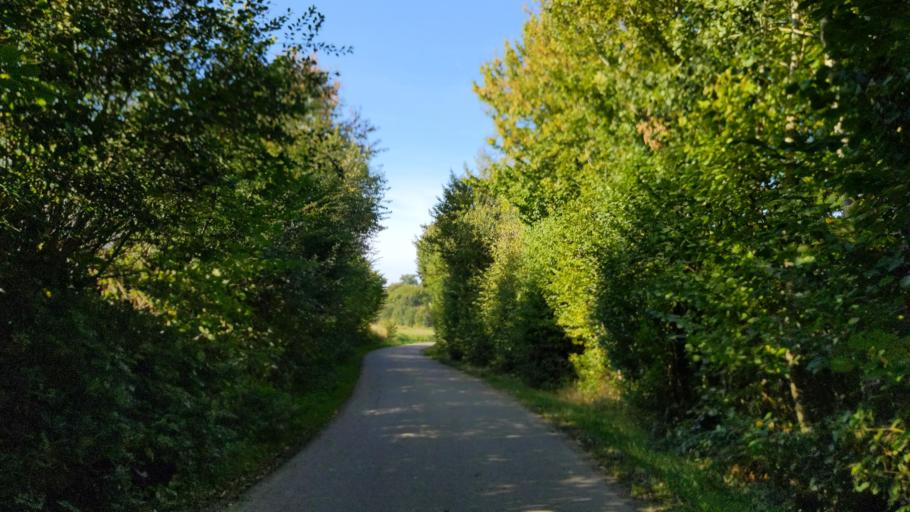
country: DE
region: Schleswig-Holstein
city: Ahrensbok
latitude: 54.0540
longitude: 10.5924
